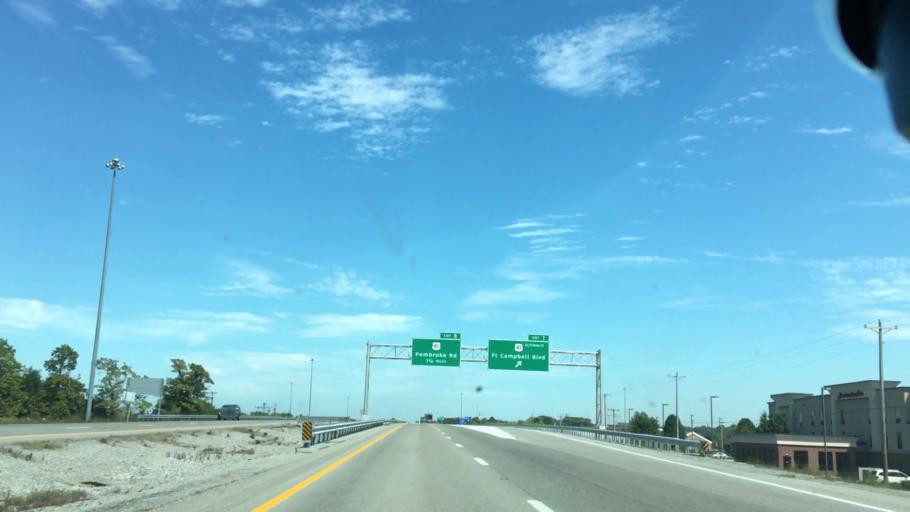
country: US
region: Kentucky
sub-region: Christian County
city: Hopkinsville
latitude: 36.8253
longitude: -87.4776
